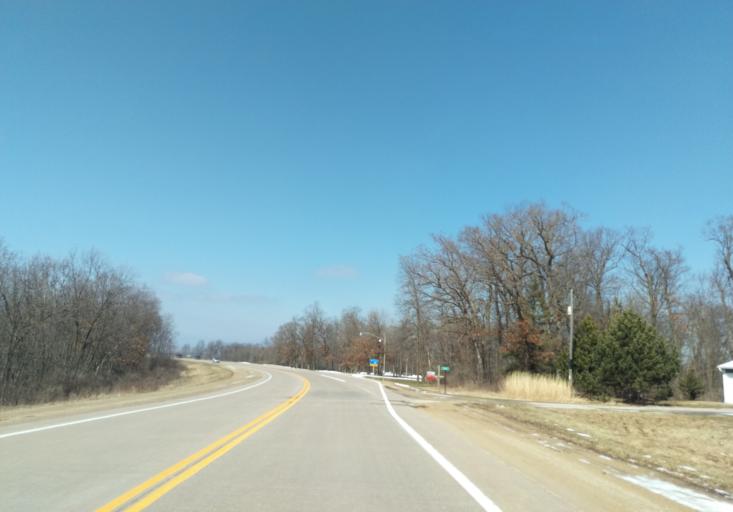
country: US
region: Wisconsin
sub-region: La Crosse County
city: La Crosse
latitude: 43.7272
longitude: -91.0878
